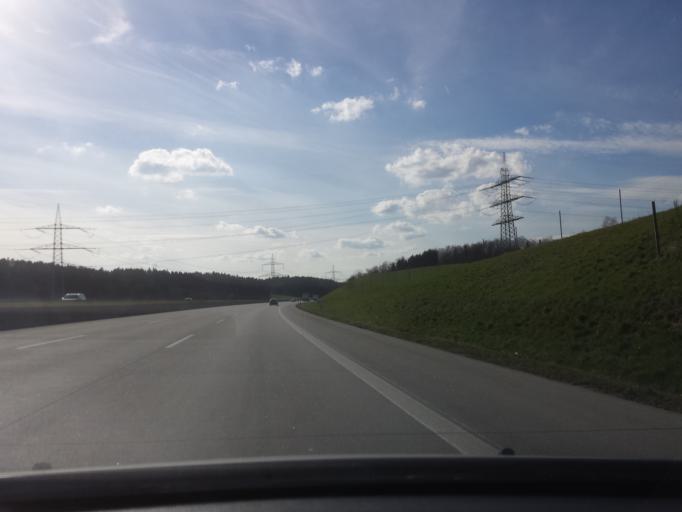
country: DE
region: Bavaria
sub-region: Swabia
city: Dasing
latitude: 48.3961
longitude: 11.0358
